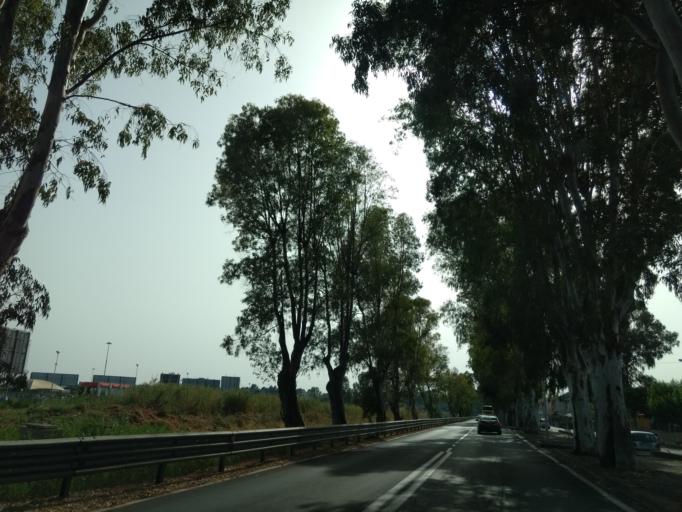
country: IT
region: Sicily
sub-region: Catania
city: Catania
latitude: 37.4741
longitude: 15.0721
